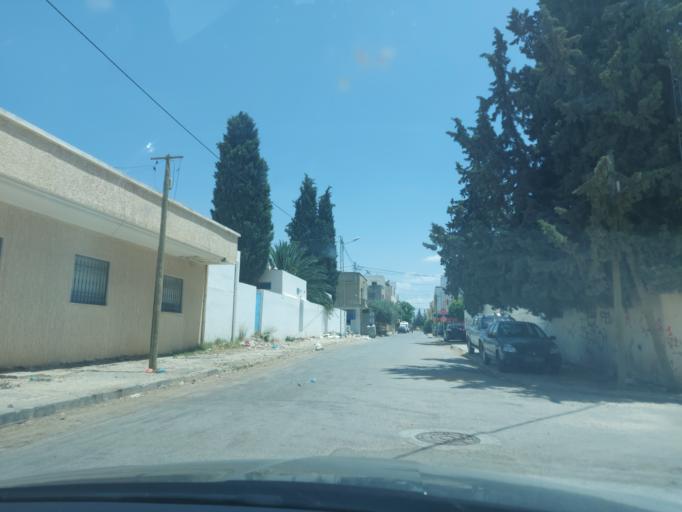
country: TN
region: Silyanah
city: Siliana
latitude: 36.0869
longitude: 9.3666
